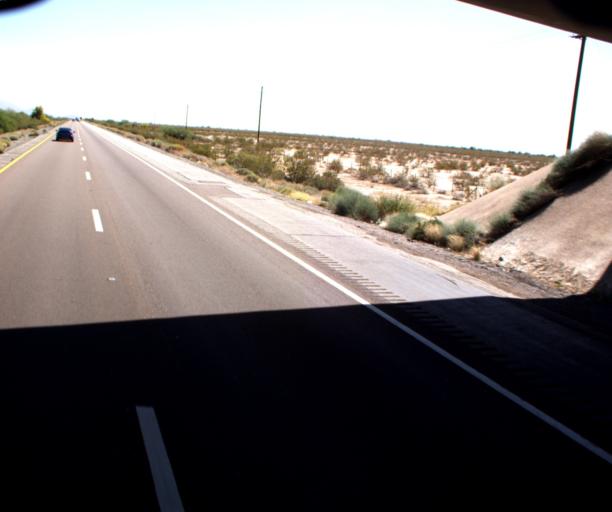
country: US
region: Arizona
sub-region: La Paz County
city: Salome
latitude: 33.5608
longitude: -113.3005
